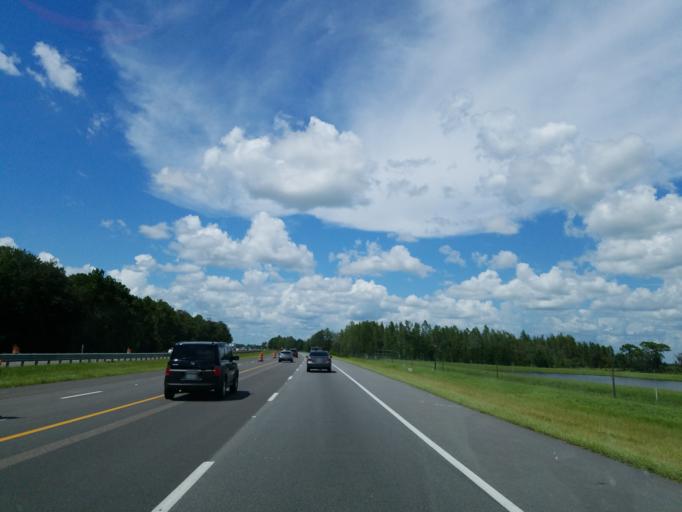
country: US
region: Florida
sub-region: Pasco County
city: Wesley Chapel
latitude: 28.2952
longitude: -82.3246
